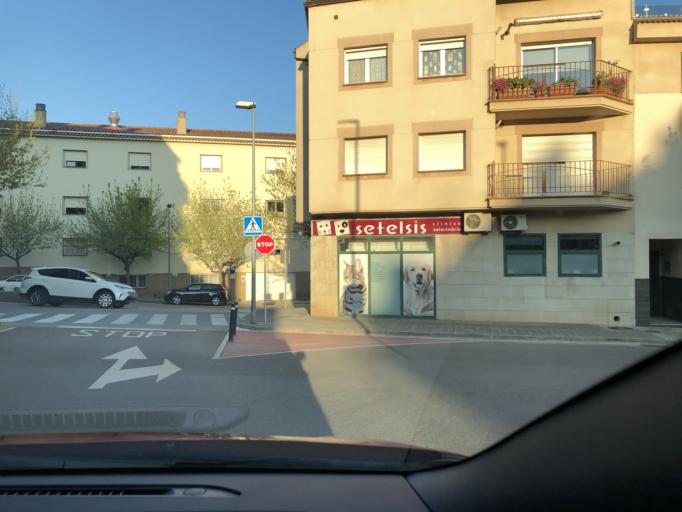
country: ES
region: Catalonia
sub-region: Provincia de Lleida
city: Solsona
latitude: 41.9926
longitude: 1.5149
